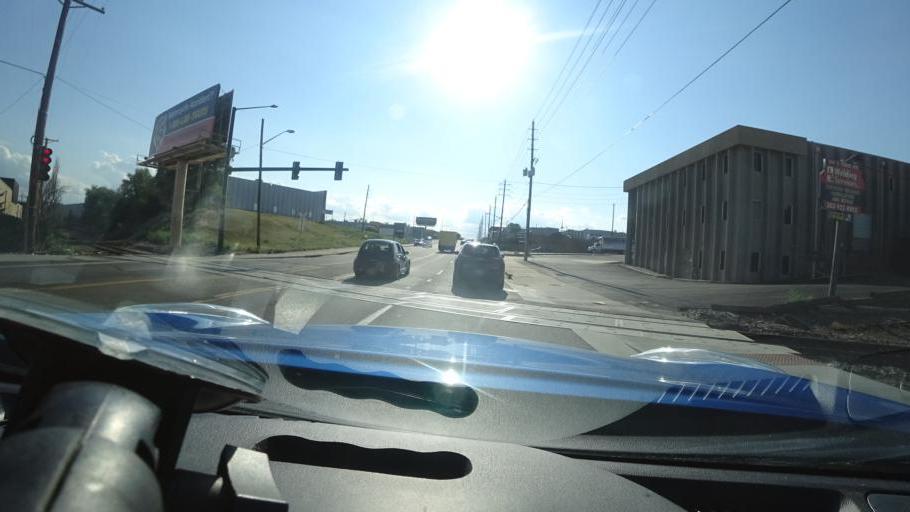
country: US
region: Colorado
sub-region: Arapahoe County
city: Englewood
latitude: 39.6786
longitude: -105.0033
